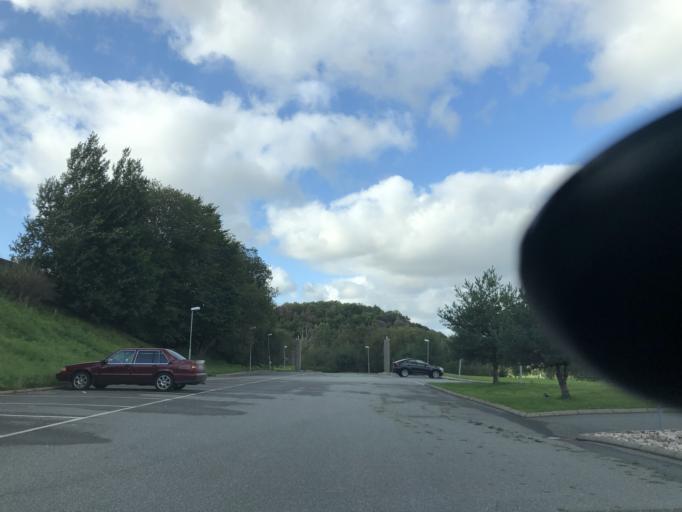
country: SE
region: Vaestra Goetaland
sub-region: Goteborg
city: Goeteborg
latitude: 57.7401
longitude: 11.9474
